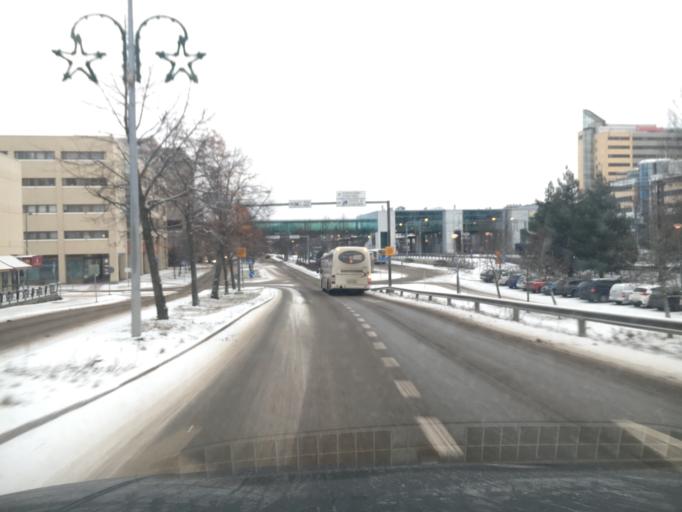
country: FI
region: Uusimaa
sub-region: Helsinki
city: Espoo
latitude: 60.2049
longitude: 24.6530
